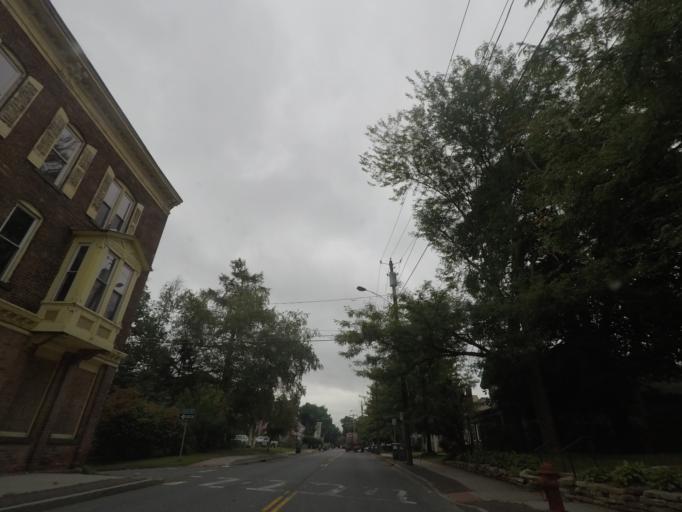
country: US
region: New York
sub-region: Rensselaer County
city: Hoosick Falls
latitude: 42.8986
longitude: -73.3520
